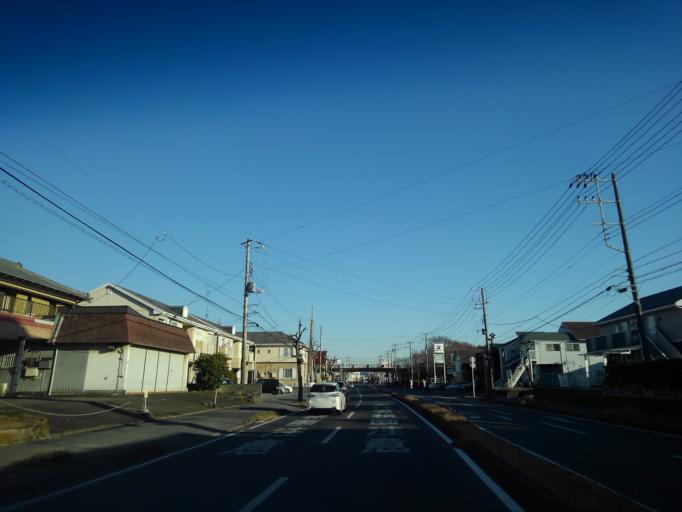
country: JP
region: Chiba
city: Kimitsu
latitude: 35.3192
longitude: 139.9174
